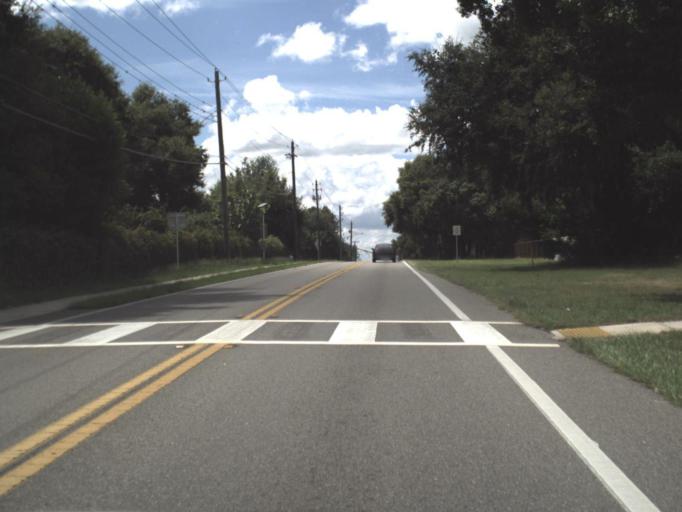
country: US
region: Florida
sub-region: Polk County
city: Winter Haven
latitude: 28.0225
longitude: -81.7031
